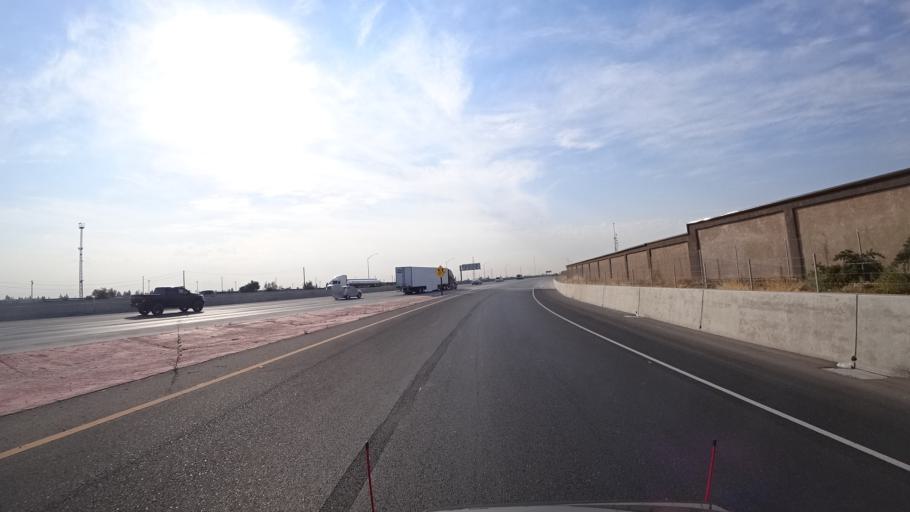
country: US
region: California
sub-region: Fresno County
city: West Park
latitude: 36.7893
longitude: -119.8580
